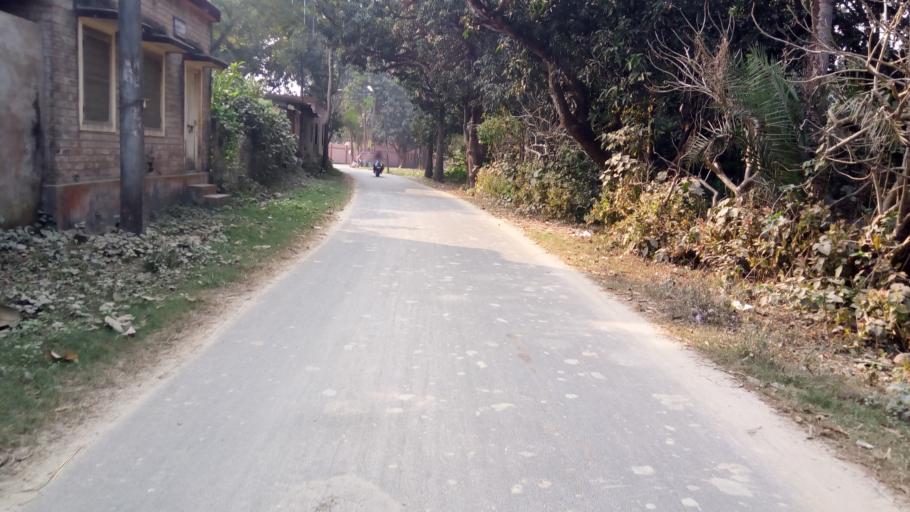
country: IN
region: West Bengal
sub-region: Nadia
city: Navadwip
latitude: 23.4476
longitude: 88.4171
